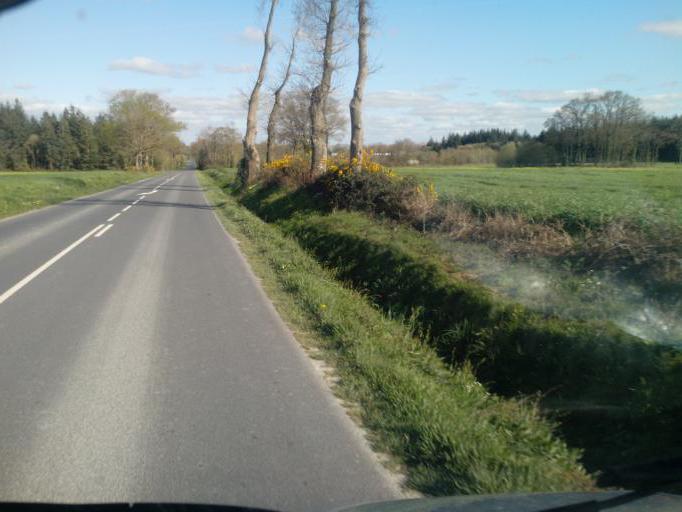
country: FR
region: Brittany
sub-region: Departement d'Ille-et-Vilaine
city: Guignen
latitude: 47.8730
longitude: -1.9088
